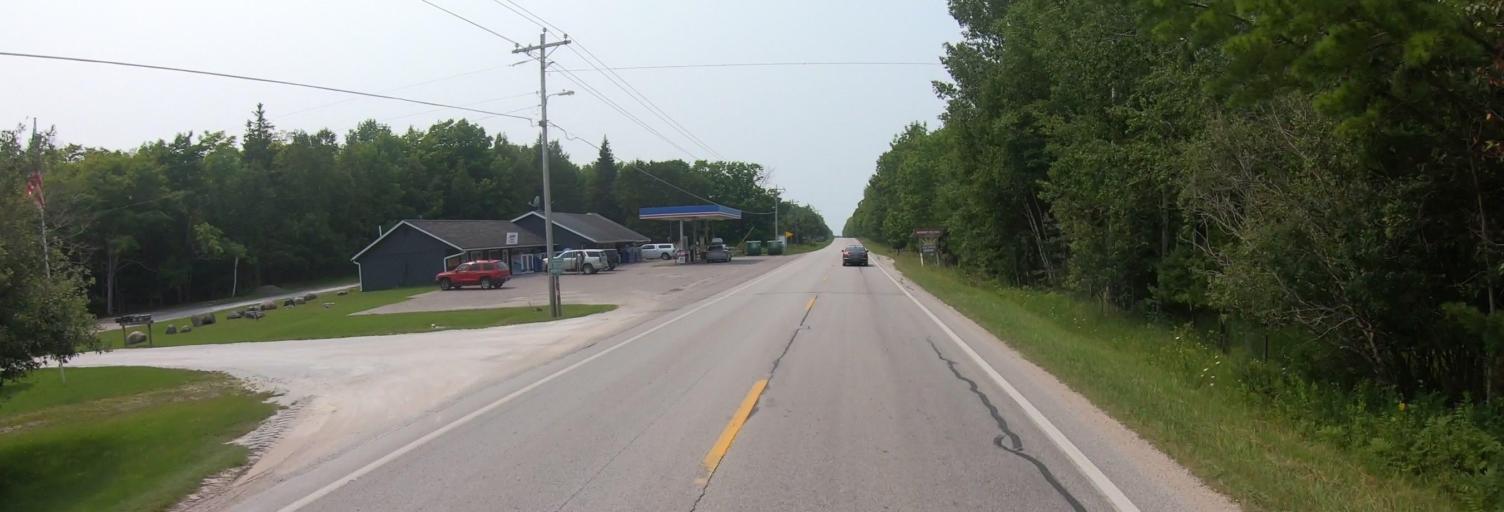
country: CA
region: Ontario
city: Thessalon
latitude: 45.9989
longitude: -83.7456
